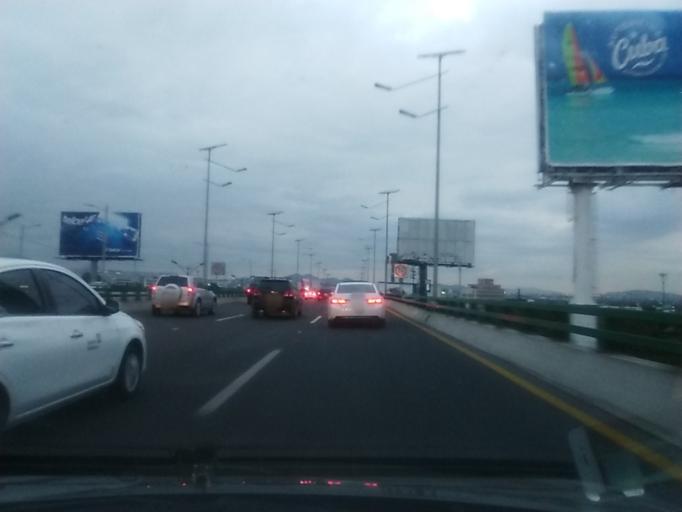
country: MX
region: Mexico
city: Naucalpan de Juarez
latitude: 19.4734
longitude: -99.2286
